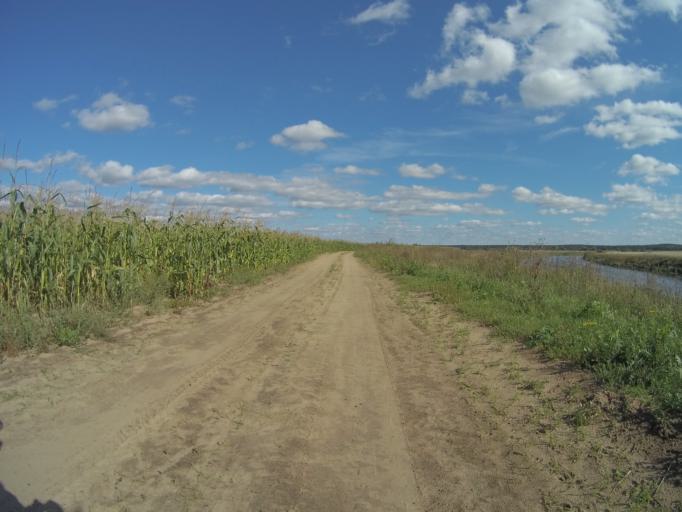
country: RU
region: Vladimir
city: Orgtrud
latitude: 56.3105
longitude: 40.6593
